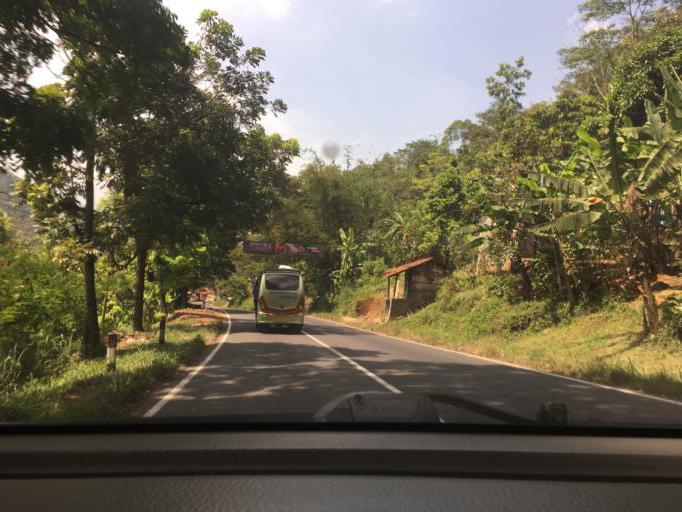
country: ID
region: West Java
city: Tagog
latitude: -7.1168
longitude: 108.1263
